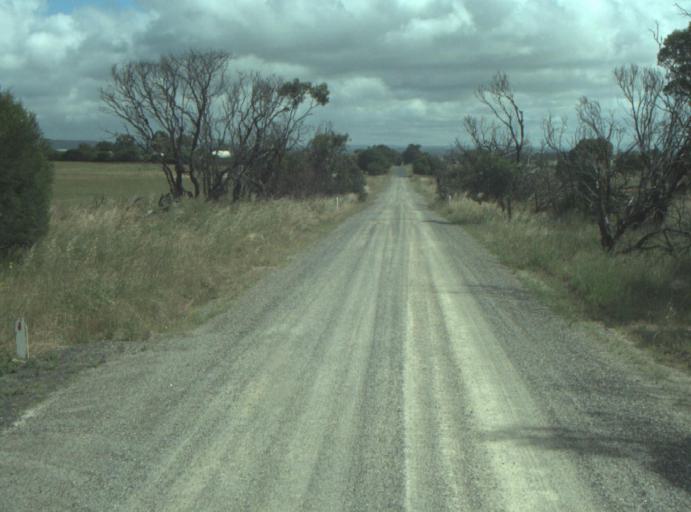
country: AU
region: Victoria
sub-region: Greater Geelong
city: Lara
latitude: -37.8670
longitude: 144.3240
